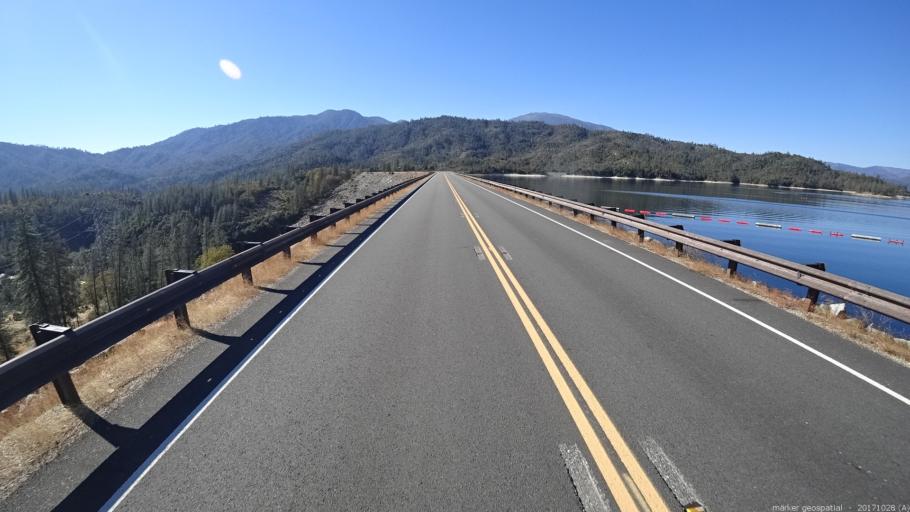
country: US
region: California
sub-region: Shasta County
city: Shasta
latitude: 40.5998
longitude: -122.5368
